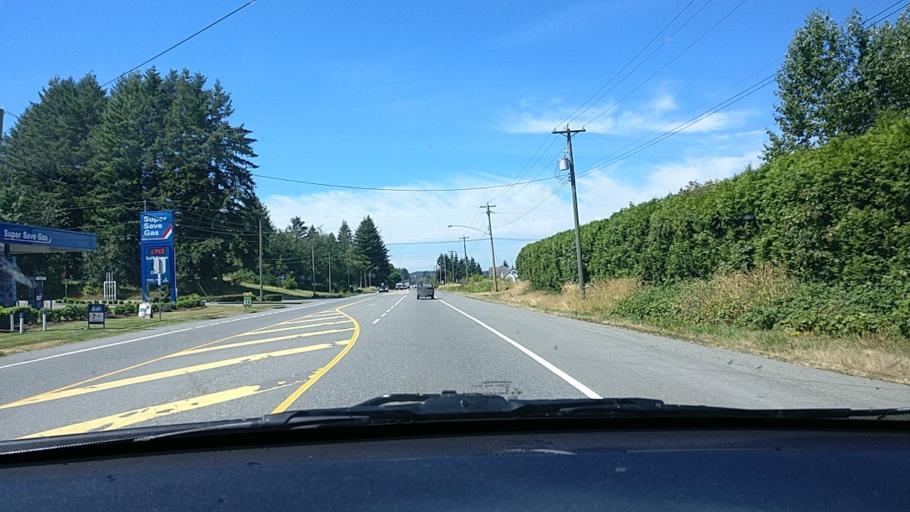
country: CA
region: British Columbia
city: Aldergrove
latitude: 49.0572
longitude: -122.4392
